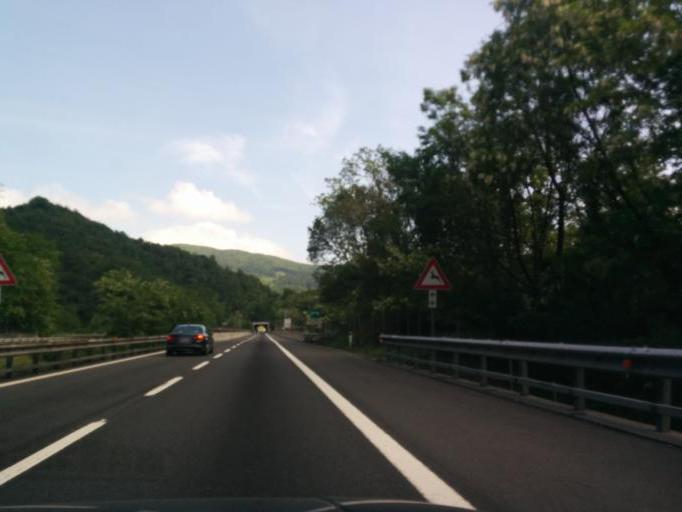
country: IT
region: Tuscany
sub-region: Provincia di Prato
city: Mercatale-San Quirico
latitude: 44.0634
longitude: 11.2089
